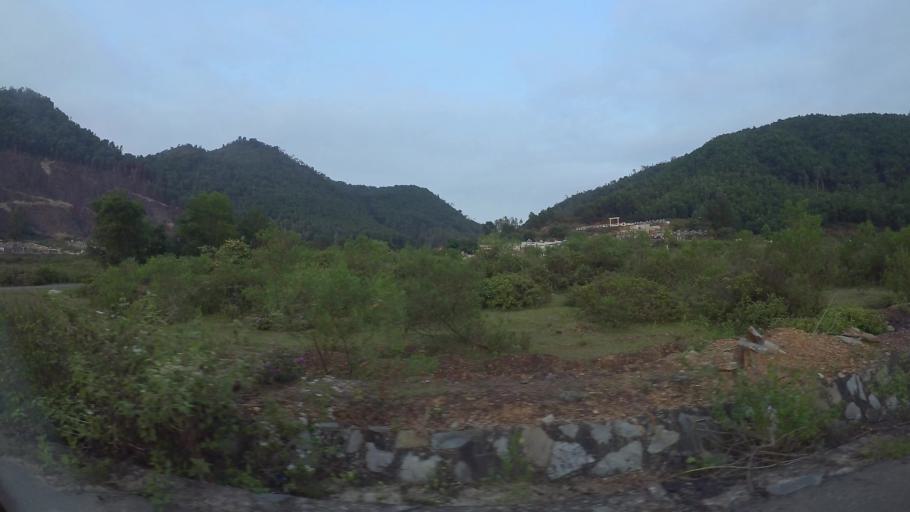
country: VN
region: Da Nang
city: Lien Chieu
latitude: 16.0588
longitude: 108.1264
